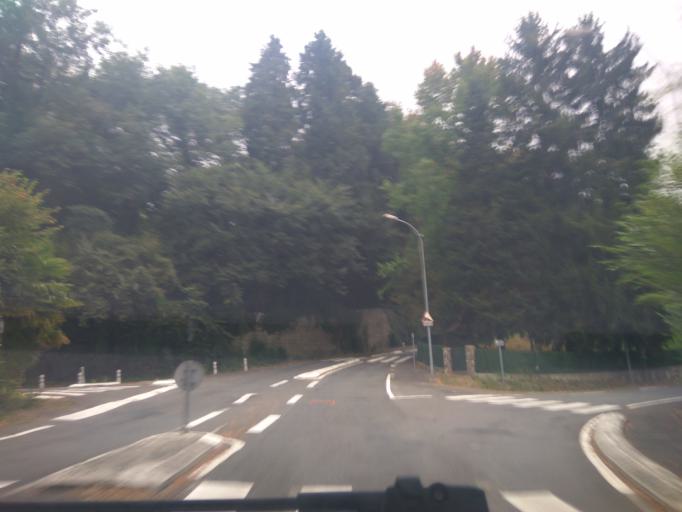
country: FR
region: Aquitaine
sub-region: Departement des Pyrenees-Atlantiques
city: Bizanos
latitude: 43.2958
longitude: -0.3363
